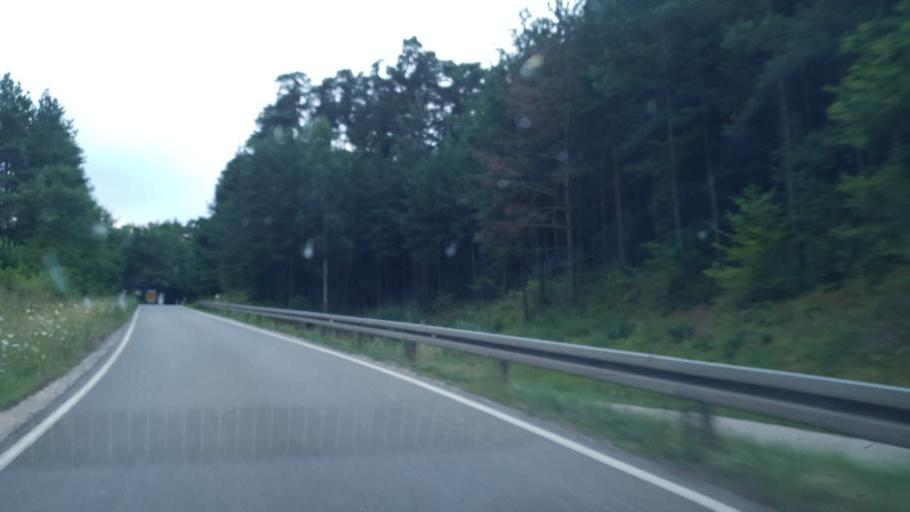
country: DE
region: Bavaria
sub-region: Regierungsbezirk Mittelfranken
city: Burgoberbach
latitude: 49.2628
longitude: 10.5880
